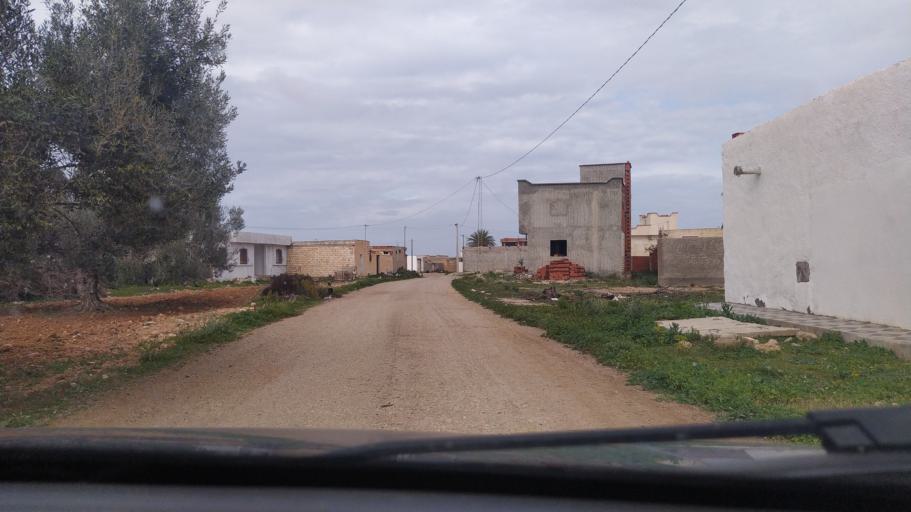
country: TN
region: Al Munastir
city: Sidi Bin Nur
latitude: 35.5173
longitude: 10.9275
